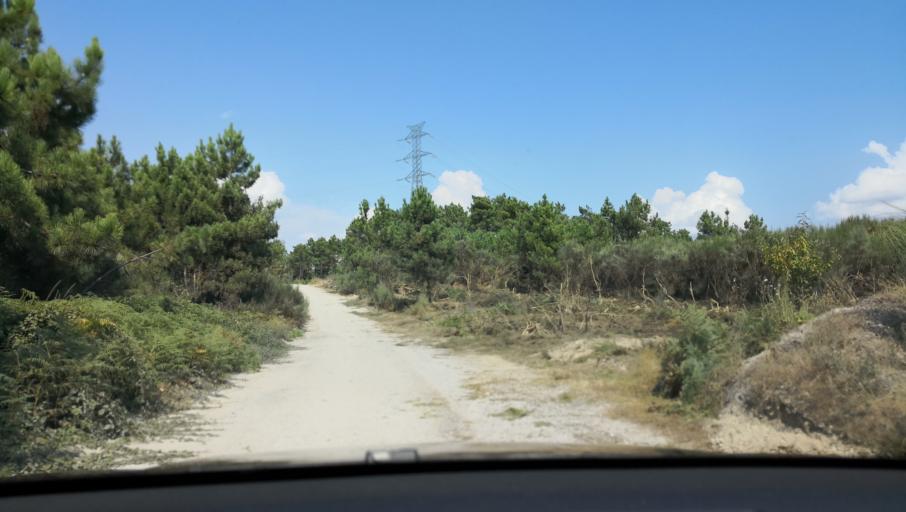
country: PT
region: Vila Real
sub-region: Sabrosa
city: Sabrosa
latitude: 41.3208
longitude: -7.6205
